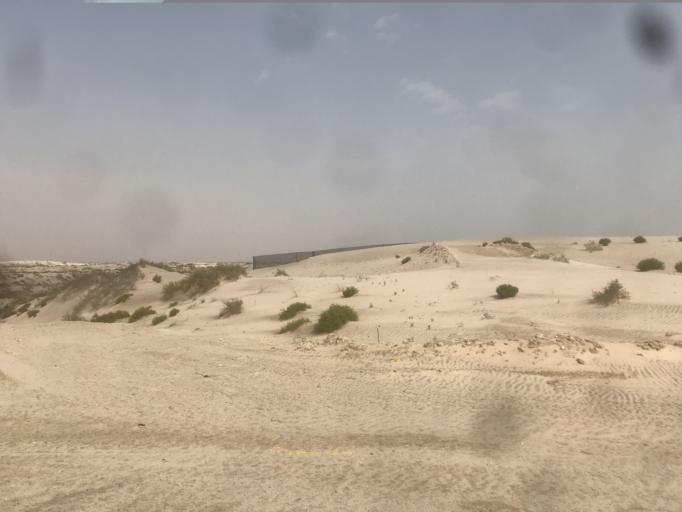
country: SA
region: Eastern Province
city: Abqaiq
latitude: 25.9072
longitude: 49.9966
